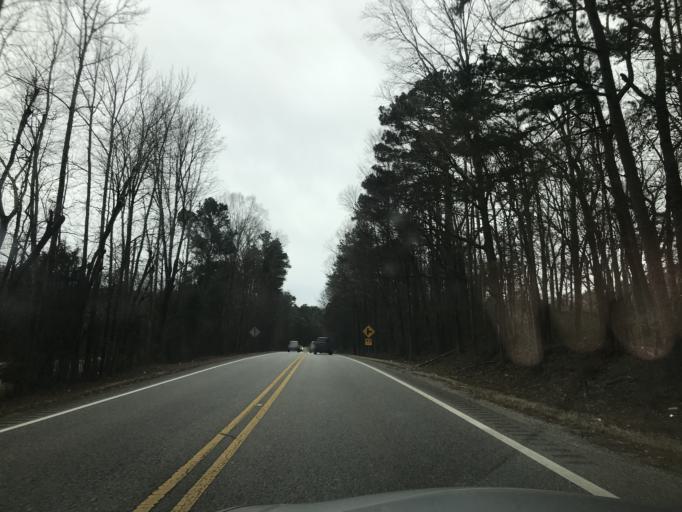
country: US
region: Alabama
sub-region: Shelby County
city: Meadowbrook
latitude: 33.4034
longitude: -86.6825
